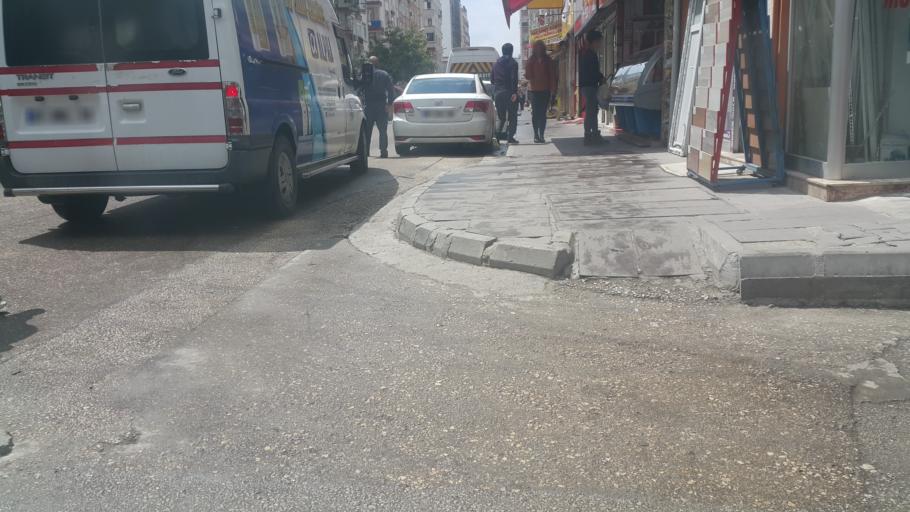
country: TR
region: Mersin
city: Mercin
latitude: 36.8056
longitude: 34.6268
